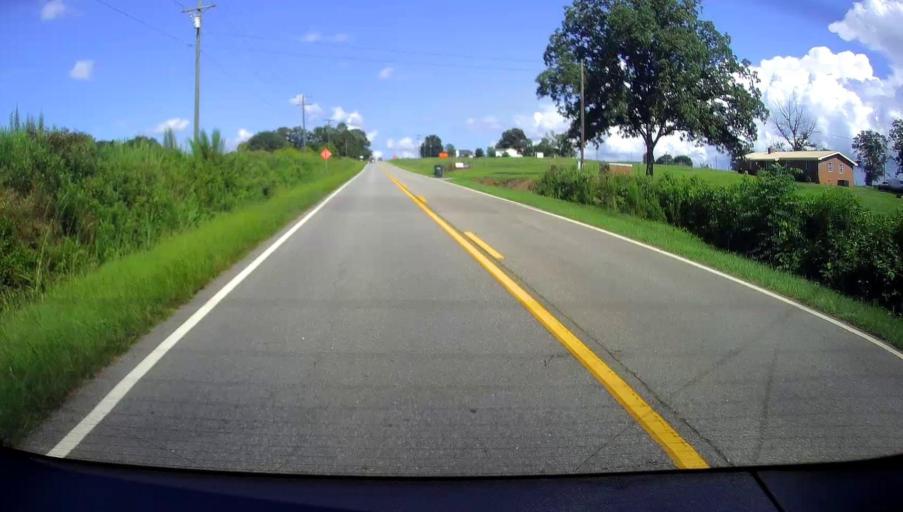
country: US
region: Georgia
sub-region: Upson County
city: Hannahs Mill
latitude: 32.9506
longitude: -84.2939
